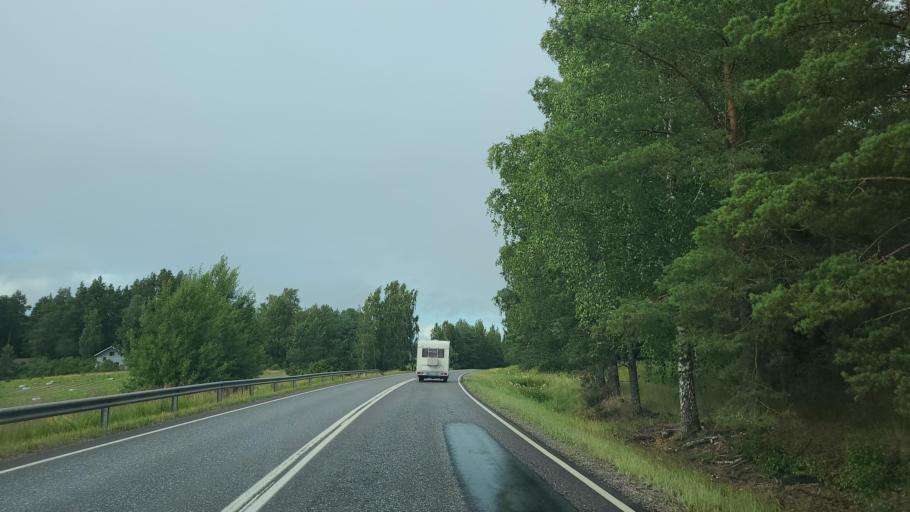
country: FI
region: Varsinais-Suomi
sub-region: Turku
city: Sauvo
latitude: 60.3101
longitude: 22.6879
